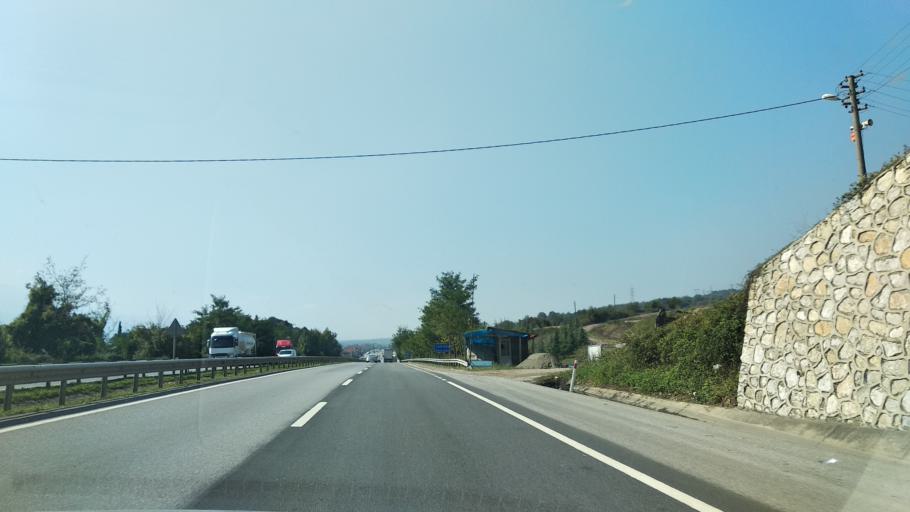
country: TR
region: Sakarya
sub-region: Merkez
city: Sapanca
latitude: 40.7352
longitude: 30.2343
